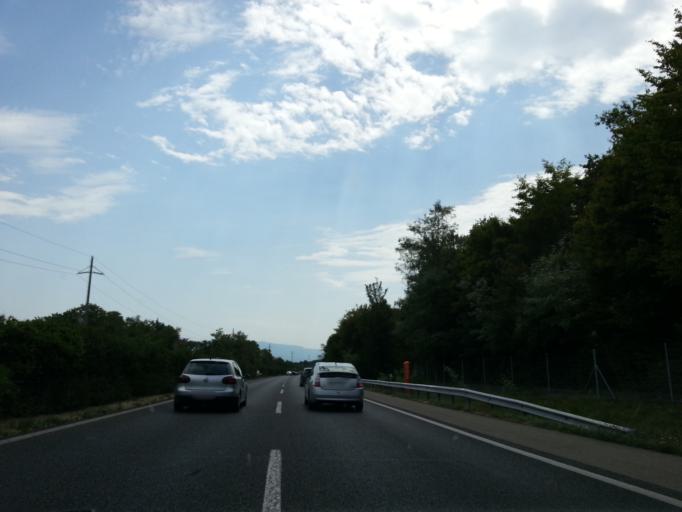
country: CH
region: Geneva
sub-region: Geneva
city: Versoix
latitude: 46.2911
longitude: 6.1461
